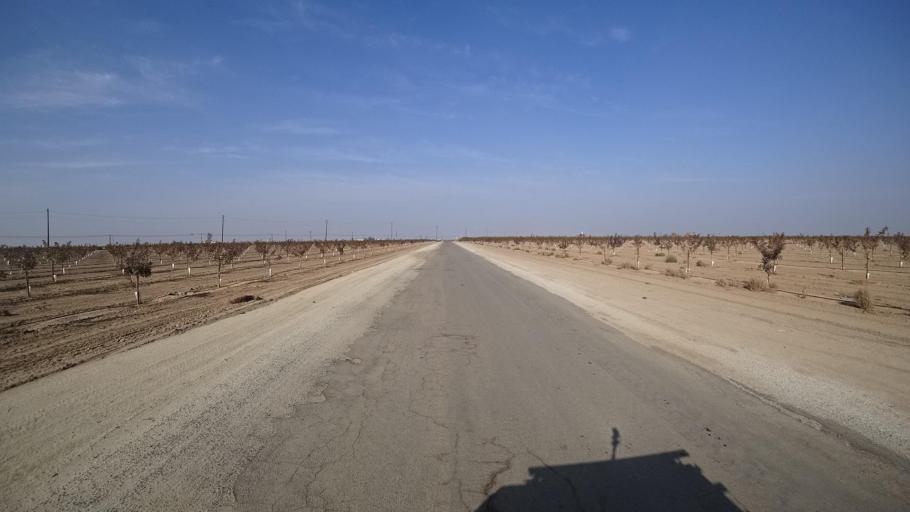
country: US
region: California
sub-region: Tulare County
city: Richgrove
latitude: 35.7845
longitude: -119.1163
